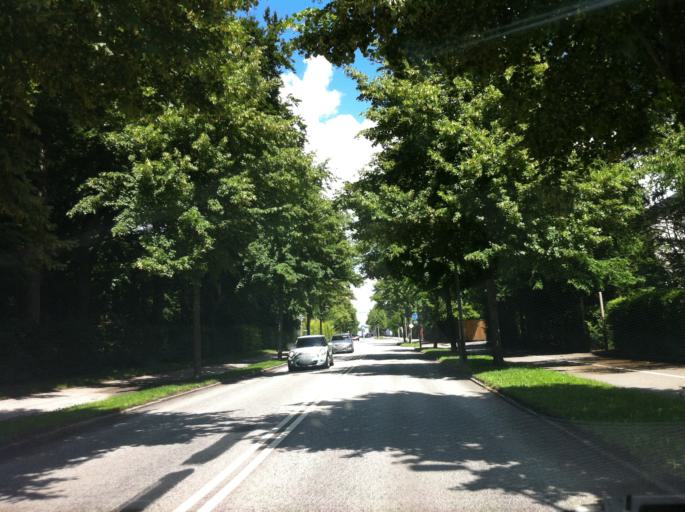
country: SE
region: Skane
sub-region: Lunds Kommun
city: Lund
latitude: 55.6855
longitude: 13.1867
